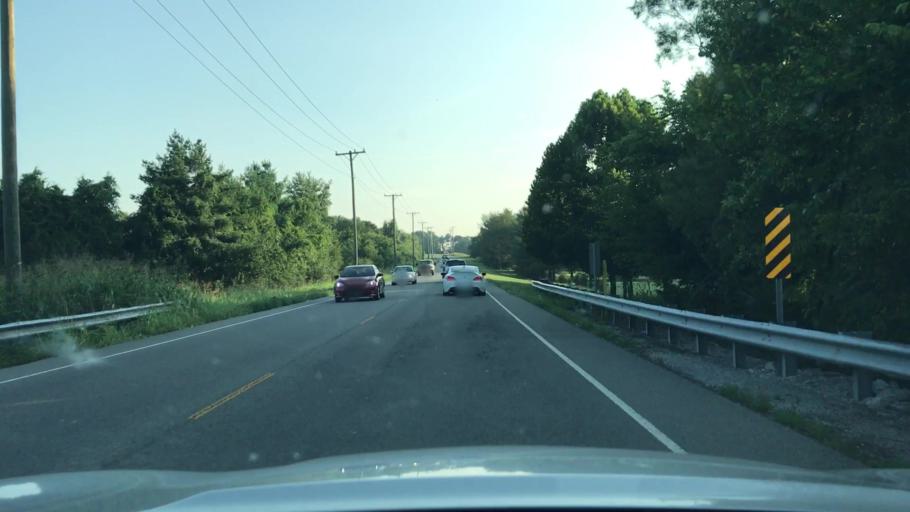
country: US
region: Tennessee
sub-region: Rutherford County
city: La Vergne
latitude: 36.0003
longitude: -86.6231
